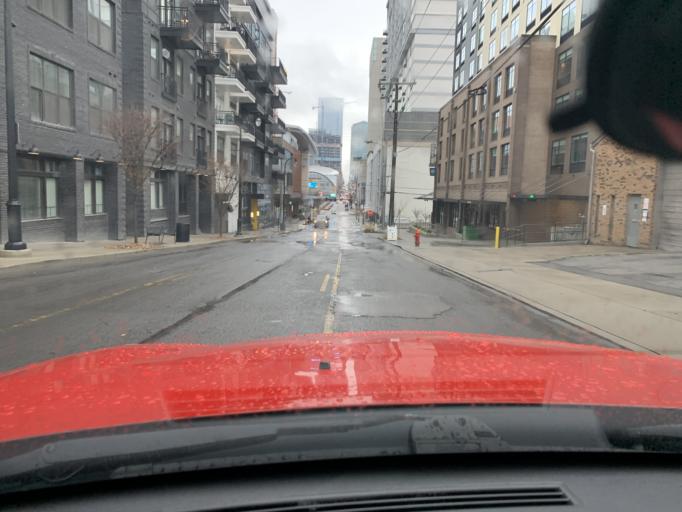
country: US
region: Tennessee
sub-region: Davidson County
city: Nashville
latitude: 36.1549
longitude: -86.7747
